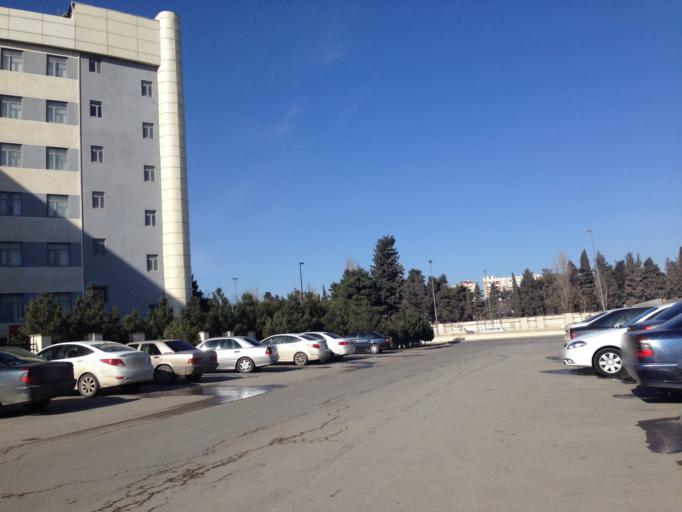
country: AZ
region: Baki
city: Baku
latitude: 40.4132
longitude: 49.8512
